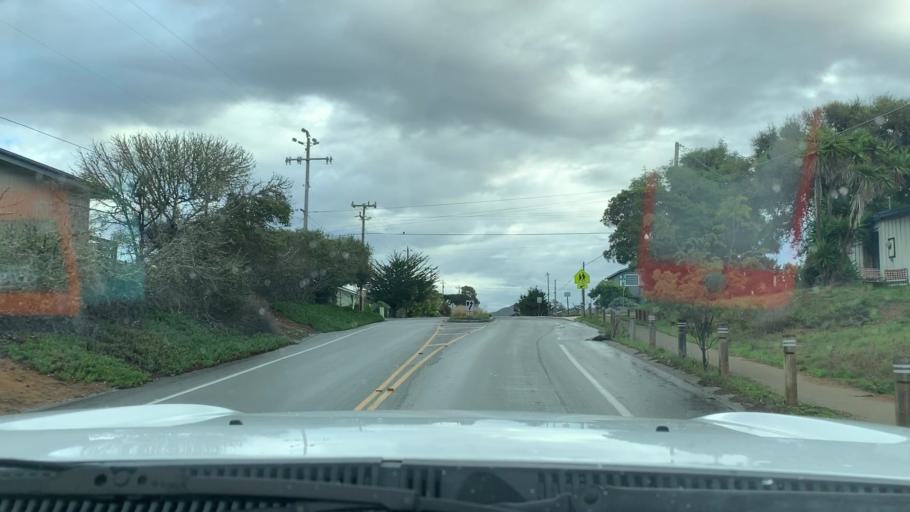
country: US
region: California
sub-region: San Luis Obispo County
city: Los Osos
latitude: 35.3300
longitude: -120.8316
